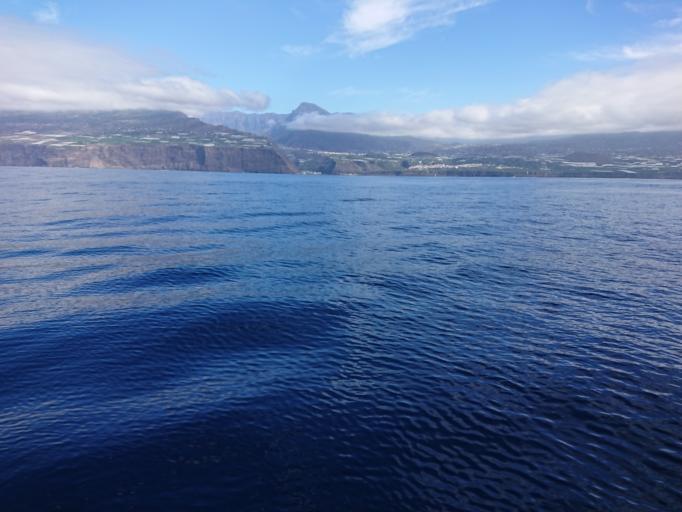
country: ES
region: Canary Islands
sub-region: Provincia de Santa Cruz de Tenerife
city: Tazacorte
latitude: 28.6250
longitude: -17.9928
